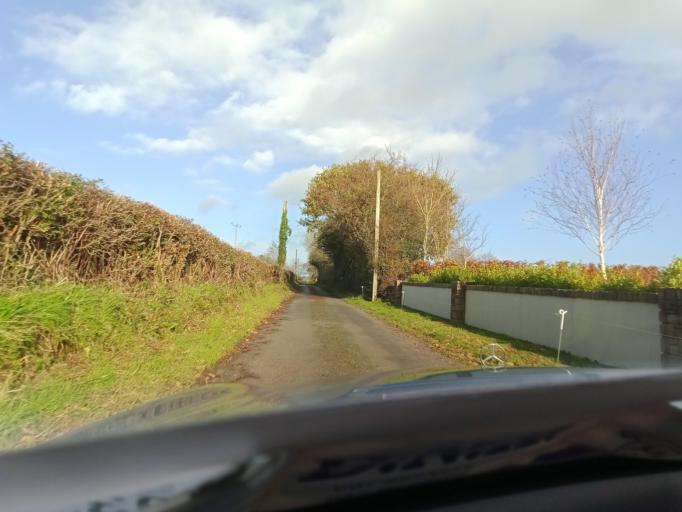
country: IE
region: Munster
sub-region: Waterford
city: Portlaw
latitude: 52.3196
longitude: -7.2870
